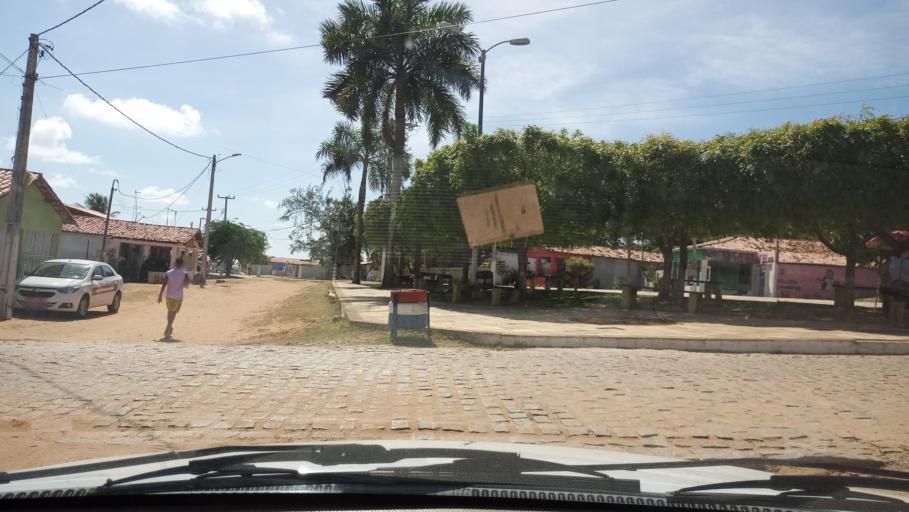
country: BR
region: Rio Grande do Norte
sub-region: Maxaranguape
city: Sao Miguel
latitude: -5.5176
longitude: -35.2619
